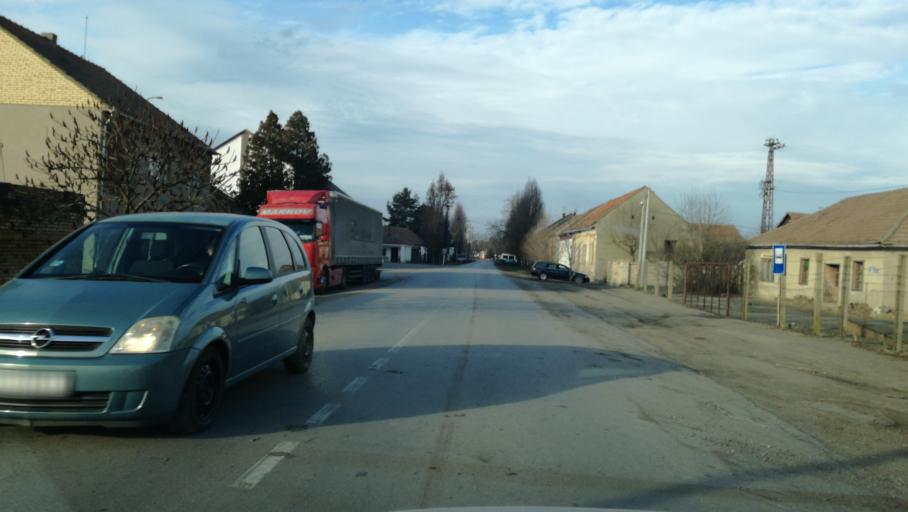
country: RS
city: Banatsko Veliko Selo
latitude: 45.8096
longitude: 20.6126
